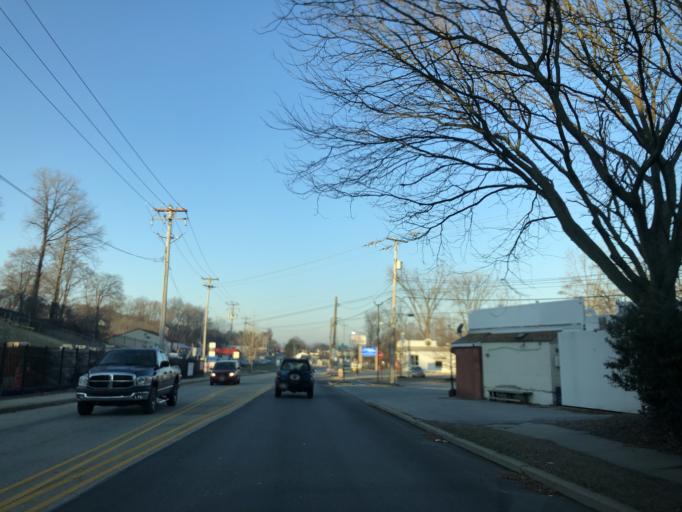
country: US
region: Pennsylvania
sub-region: Chester County
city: West Chester
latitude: 39.9591
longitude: -75.6130
